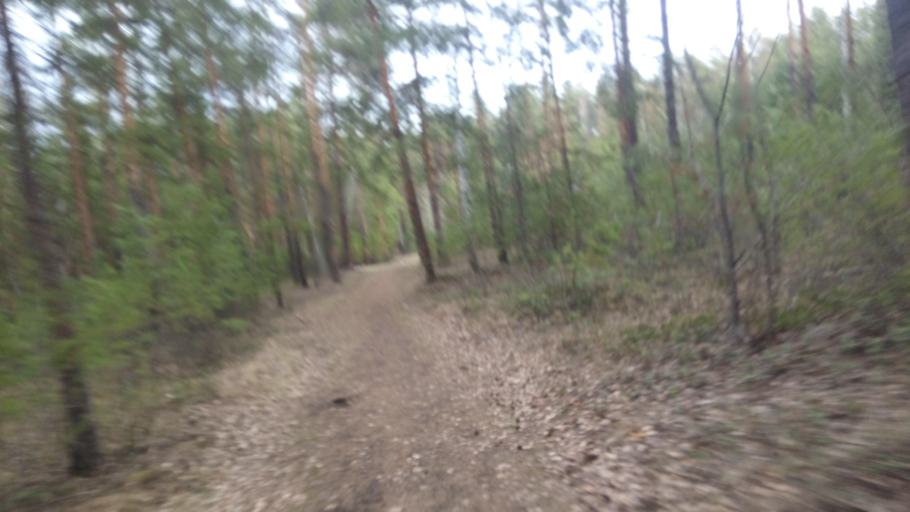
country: RU
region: Chelyabinsk
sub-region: Gorod Chelyabinsk
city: Chelyabinsk
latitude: 55.1339
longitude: 61.3370
